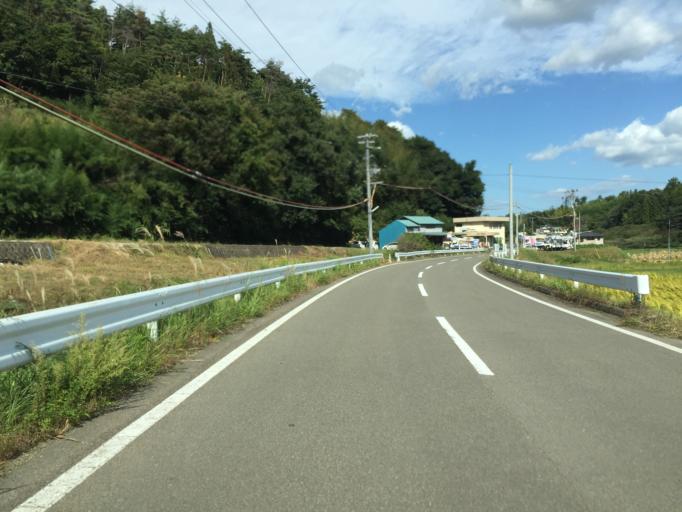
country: JP
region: Fukushima
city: Hobaramachi
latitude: 37.7786
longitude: 140.5466
